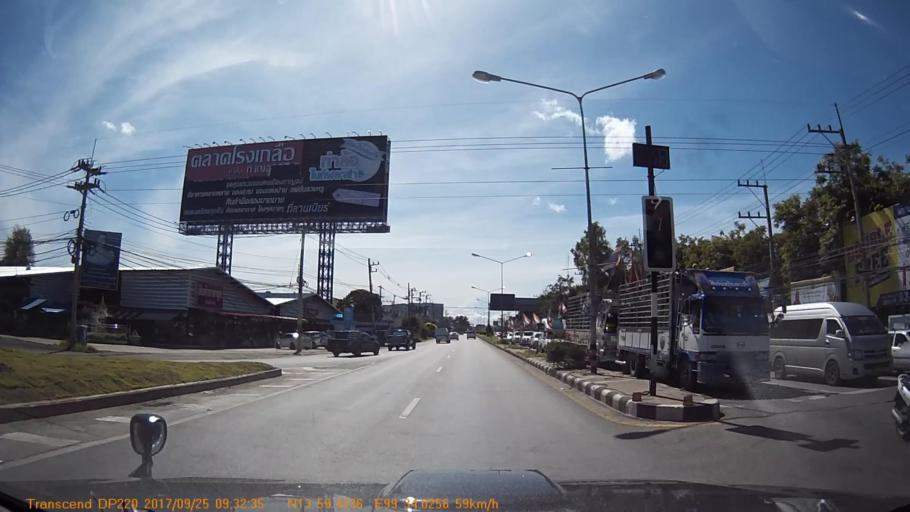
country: TH
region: Kanchanaburi
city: Kanchanaburi
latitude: 13.9904
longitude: 99.5673
